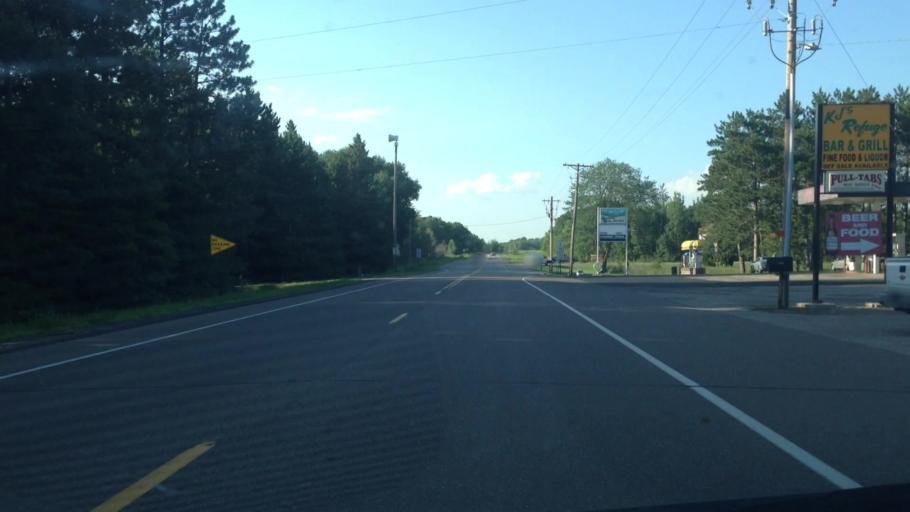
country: US
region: Minnesota
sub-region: Sherburne County
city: Big Lake
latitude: 45.4460
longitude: -93.7360
